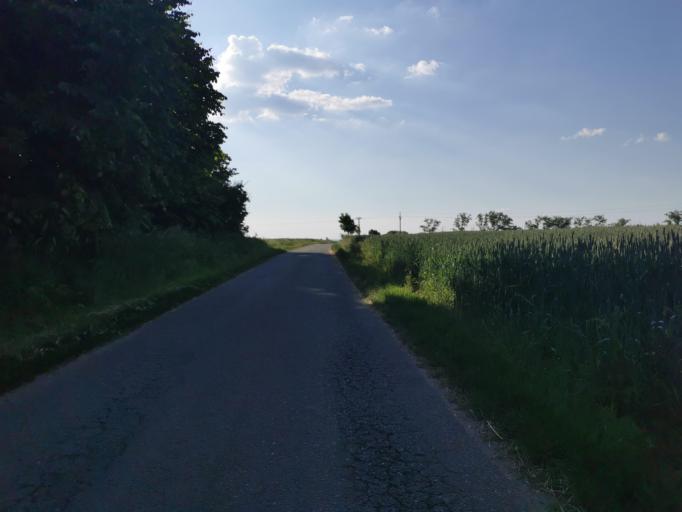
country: CZ
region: South Moravian
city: Straznice
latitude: 48.8839
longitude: 17.3433
